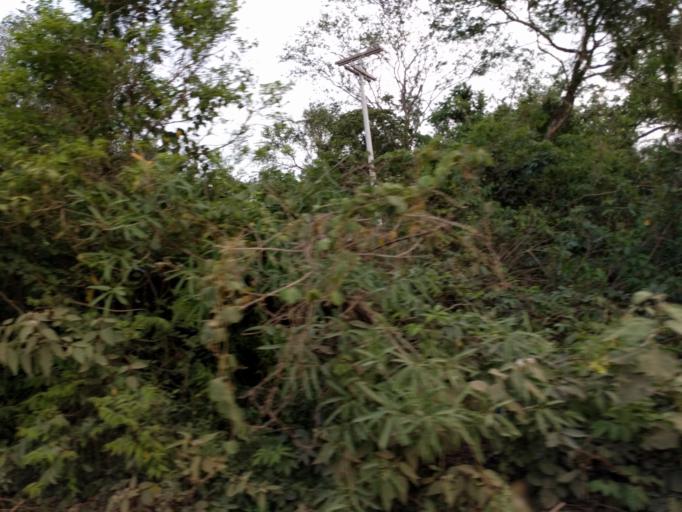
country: BO
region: Santa Cruz
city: Santa Rita
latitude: -17.9394
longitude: -63.3628
